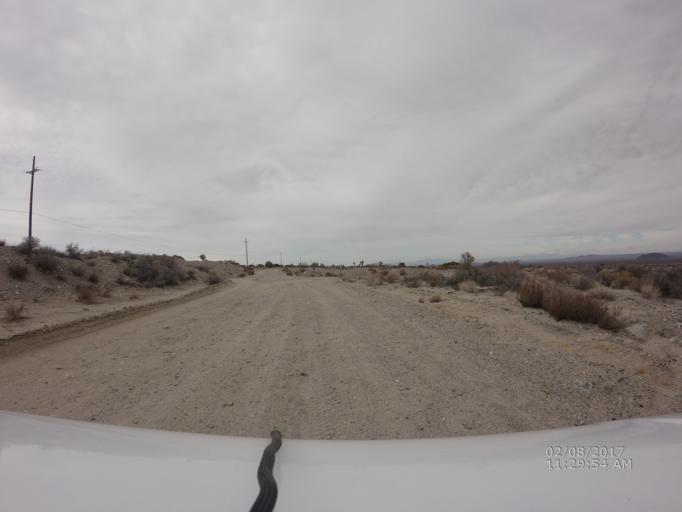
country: US
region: California
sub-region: San Bernardino County
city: Pinon Hills
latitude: 34.4638
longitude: -117.7015
